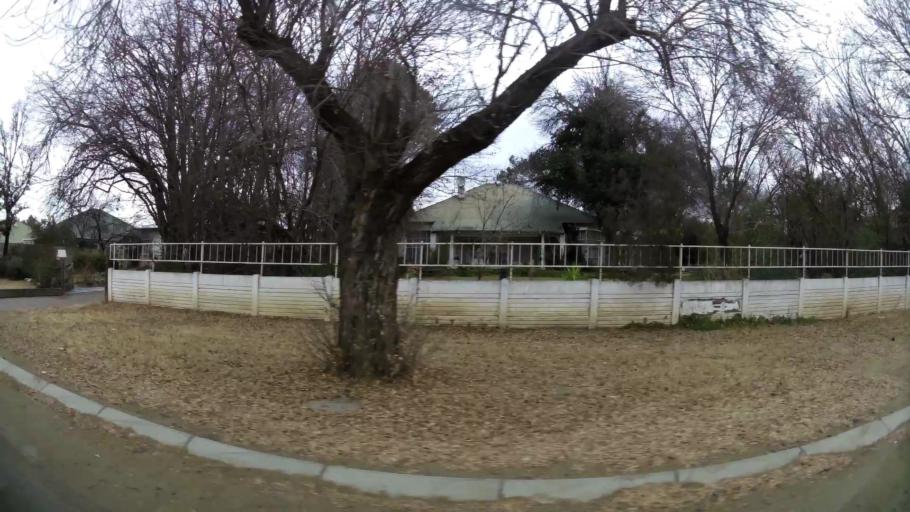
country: ZA
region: Orange Free State
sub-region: Fezile Dabi District Municipality
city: Kroonstad
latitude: -27.6589
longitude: 27.2470
